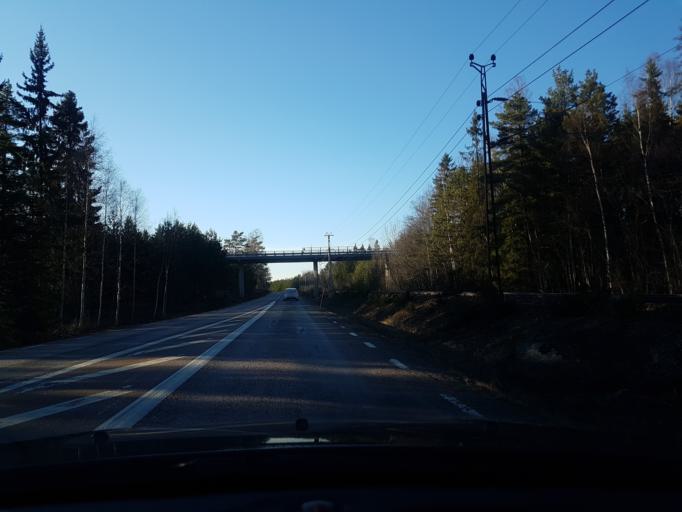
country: SE
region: Vaestmanland
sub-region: Sala Kommun
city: Sala
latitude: 59.9680
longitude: 16.5051
